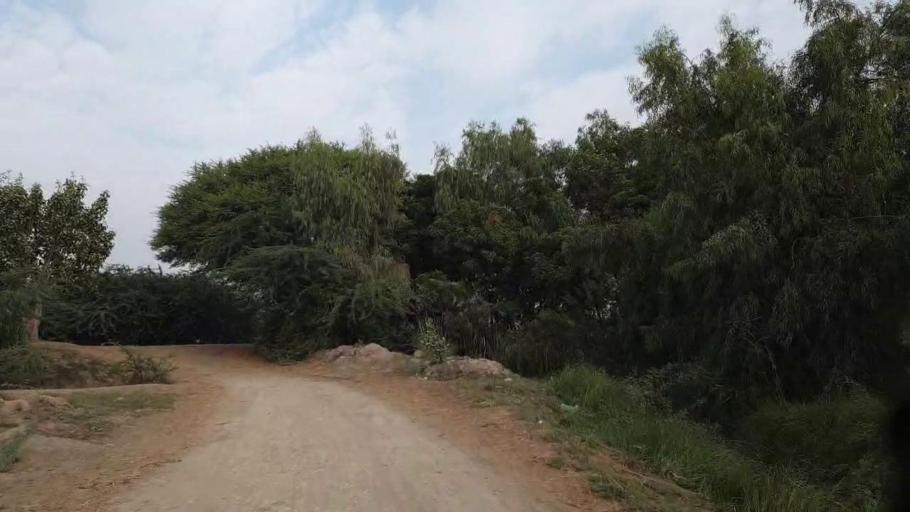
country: PK
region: Sindh
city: Tando Muhammad Khan
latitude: 25.0955
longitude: 68.4174
